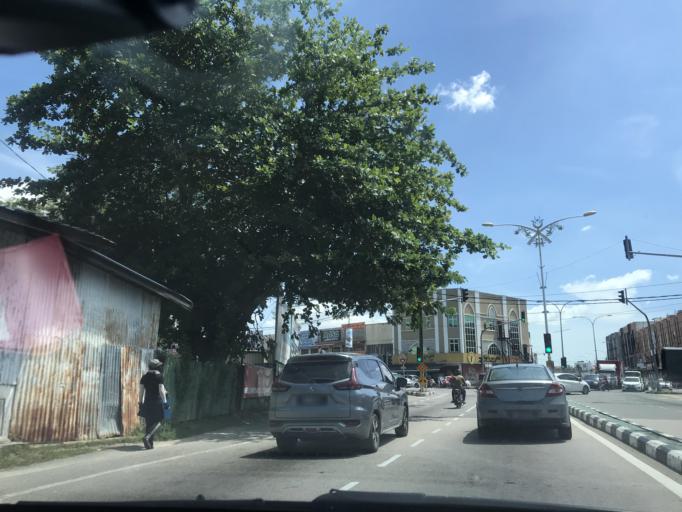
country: MY
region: Kelantan
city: Kota Bharu
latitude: 6.1089
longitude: 102.2548
